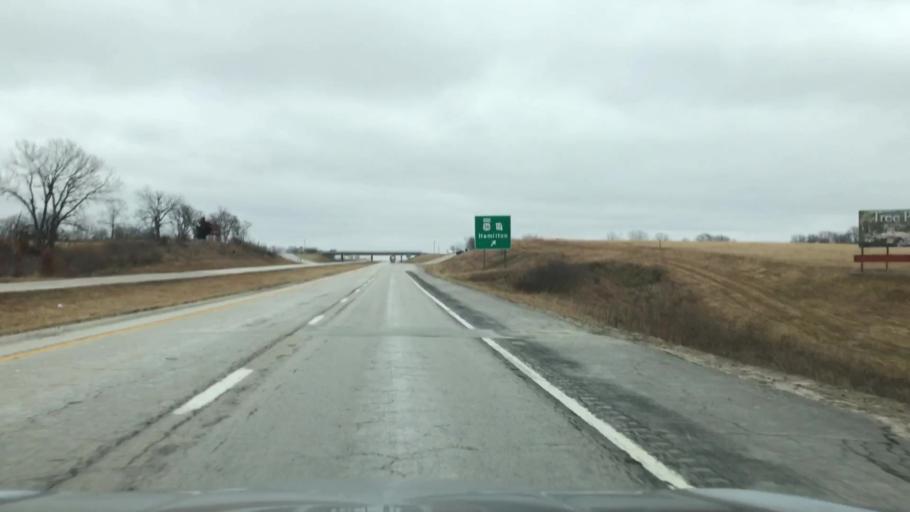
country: US
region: Missouri
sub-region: Caldwell County
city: Hamilton
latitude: 39.7333
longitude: -94.0073
